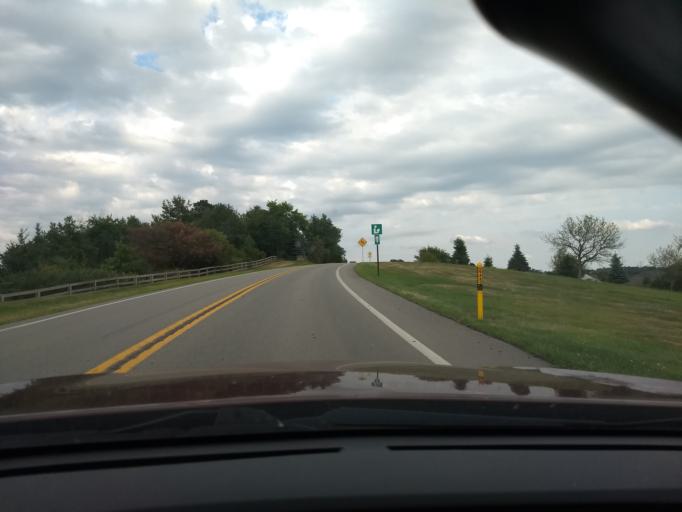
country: US
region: Pennsylvania
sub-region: Butler County
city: Mars
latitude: 40.6690
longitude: -80.0322
